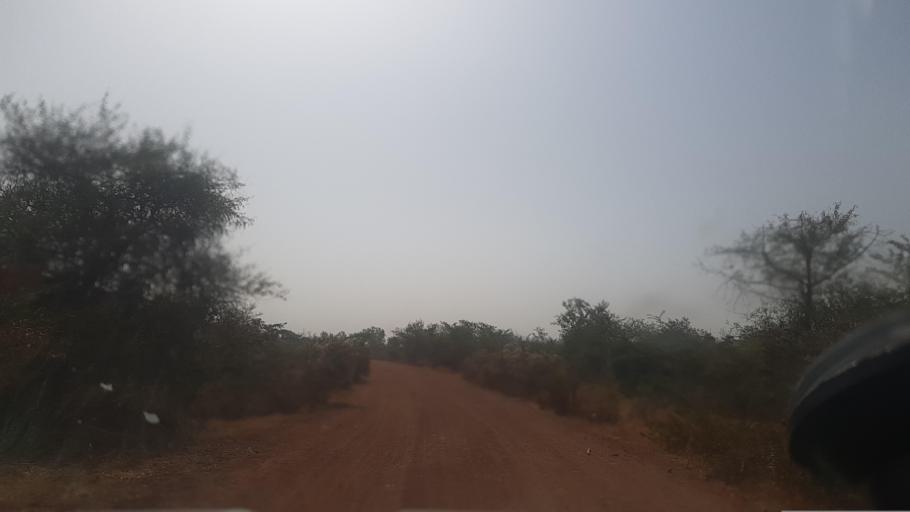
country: ML
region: Segou
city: Baroueli
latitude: 13.0799
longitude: -6.4857
